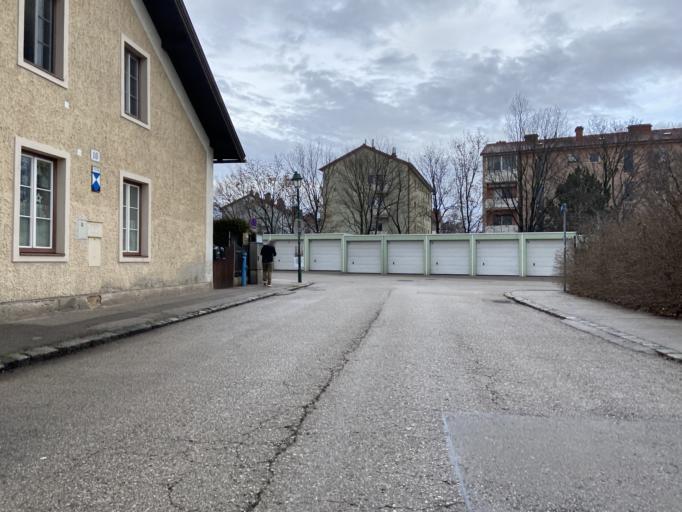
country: AT
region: Lower Austria
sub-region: Politischer Bezirk Modling
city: Wiener Neudorf
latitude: 48.0797
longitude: 16.3045
